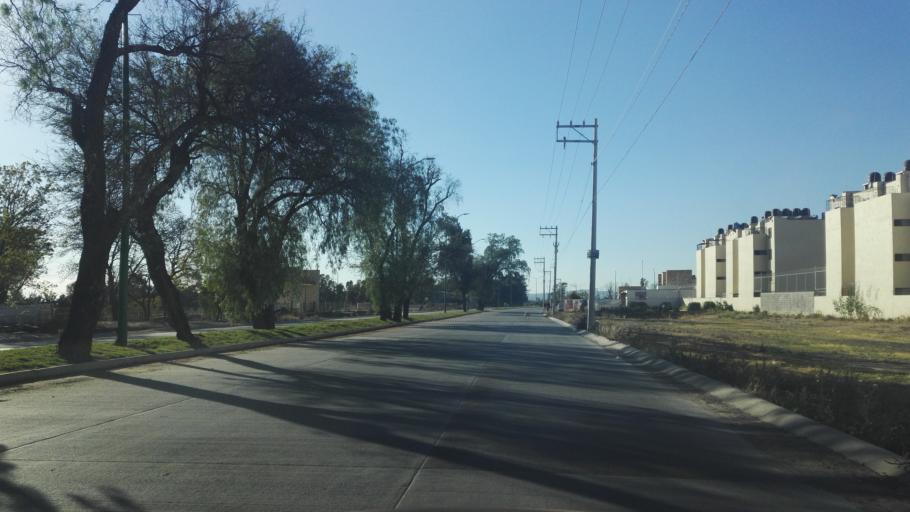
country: MX
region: Guanajuato
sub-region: Leon
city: Fraccionamiento Paraiso Real
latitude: 21.0640
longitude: -101.6073
